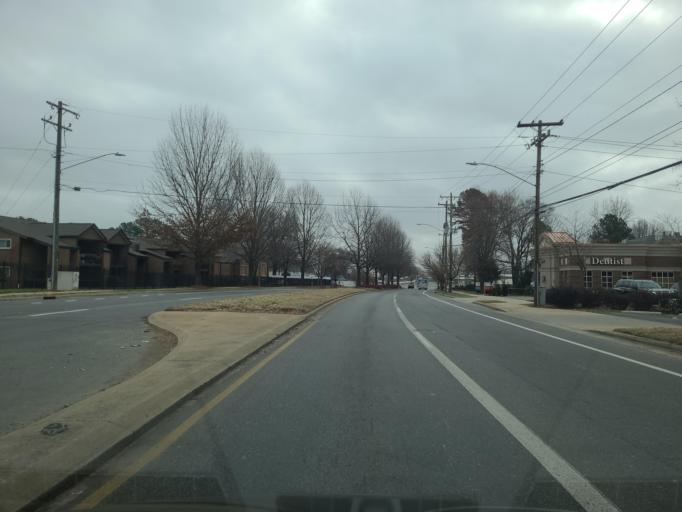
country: US
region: North Carolina
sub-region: Mecklenburg County
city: Charlotte
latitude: 35.2115
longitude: -80.7605
